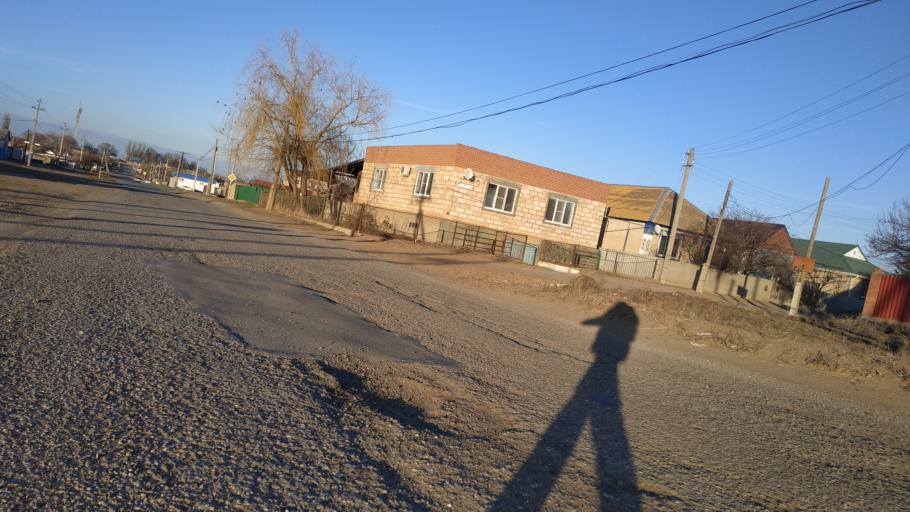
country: RU
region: Astrakhan
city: Liman
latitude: 45.7831
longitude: 47.2092
